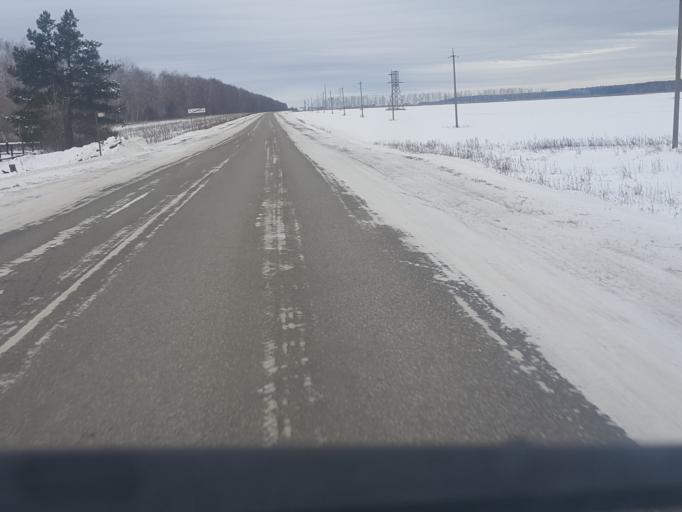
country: RU
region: Tambov
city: Platonovka
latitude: 52.8260
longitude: 41.8035
